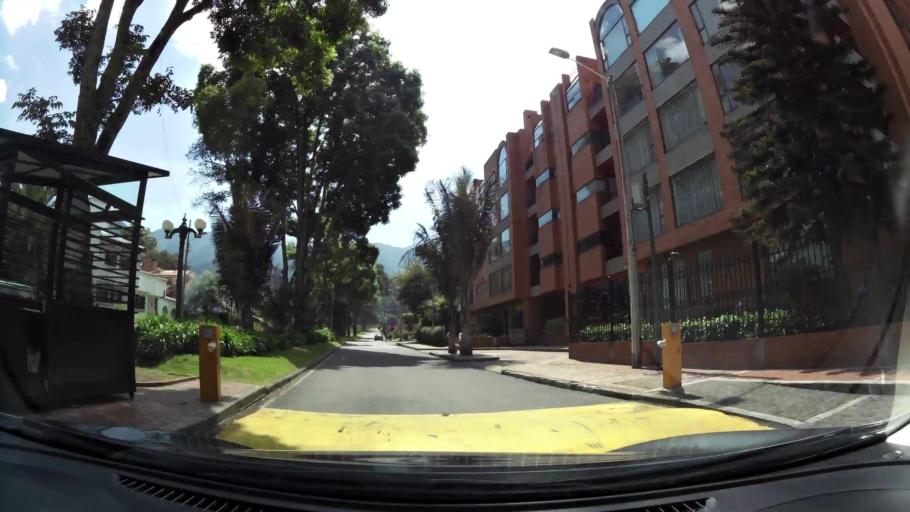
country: CO
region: Bogota D.C.
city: Barrio San Luis
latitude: 4.6875
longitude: -74.0339
